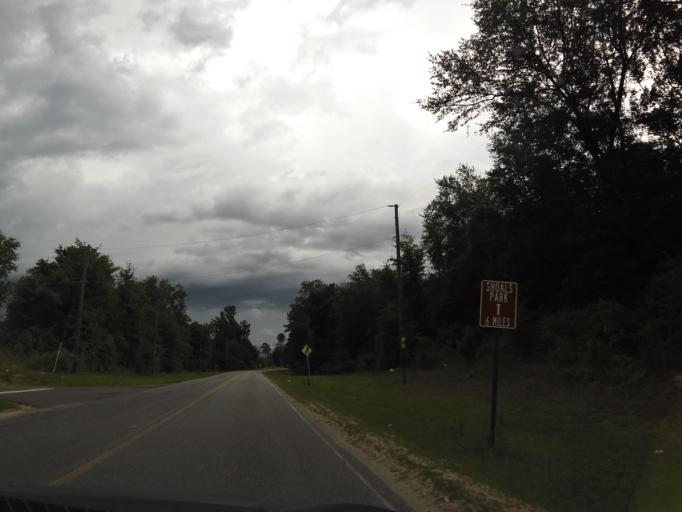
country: US
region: Florida
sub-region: Baker County
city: Macclenny
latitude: 30.2643
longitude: -82.1623
